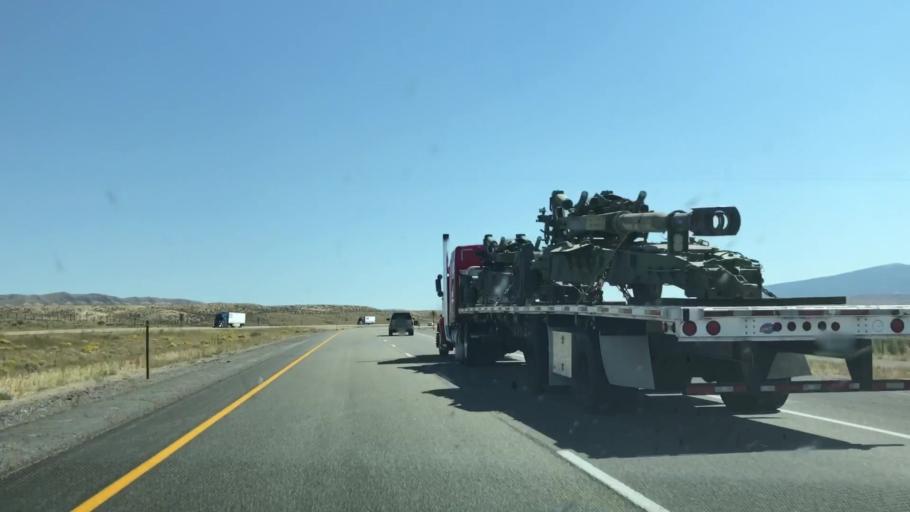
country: US
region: Wyoming
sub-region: Carbon County
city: Saratoga
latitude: 41.7411
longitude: -106.7761
